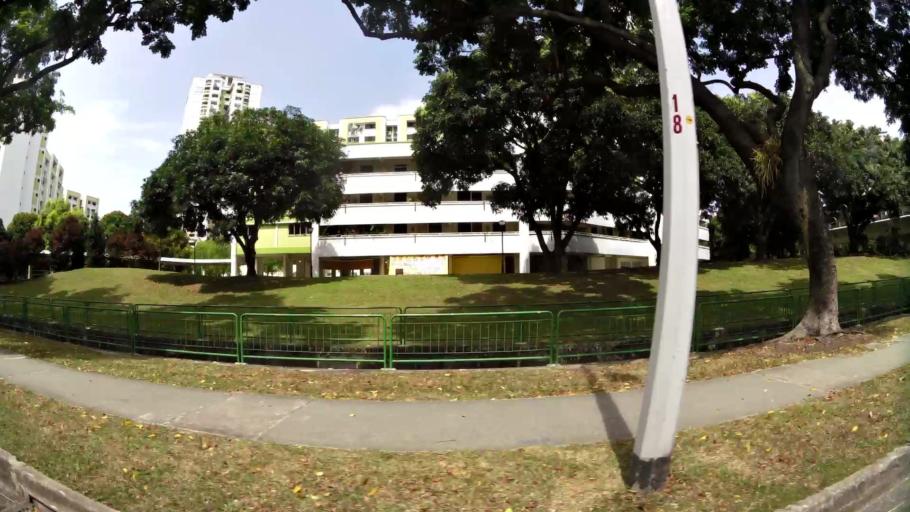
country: SG
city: Singapore
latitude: 1.3366
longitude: 103.7395
